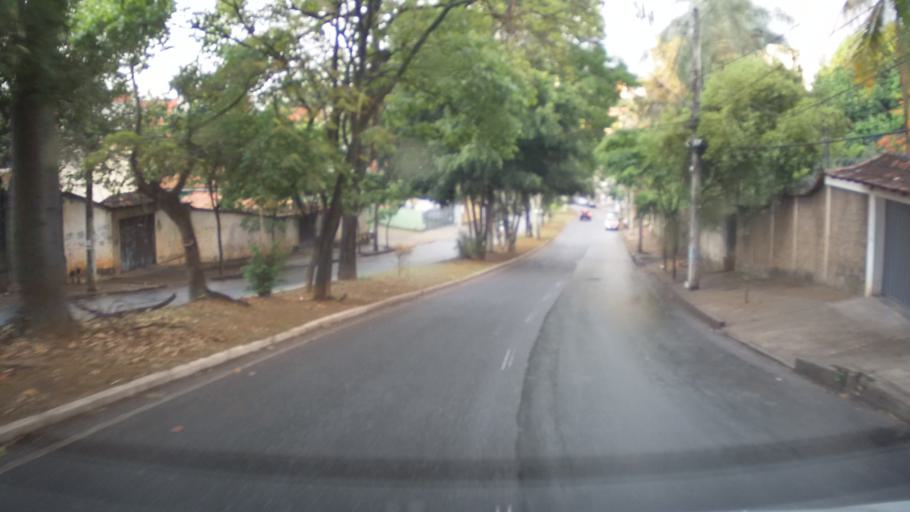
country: BR
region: Minas Gerais
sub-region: Belo Horizonte
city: Belo Horizonte
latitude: -19.9644
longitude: -43.9822
